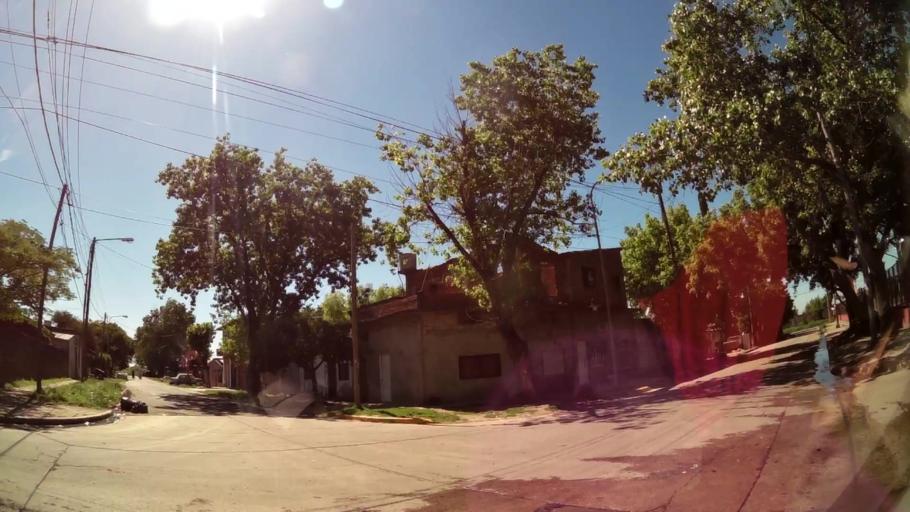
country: AR
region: Buenos Aires
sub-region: Partido de Tigre
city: Tigre
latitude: -34.5012
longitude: -58.6096
